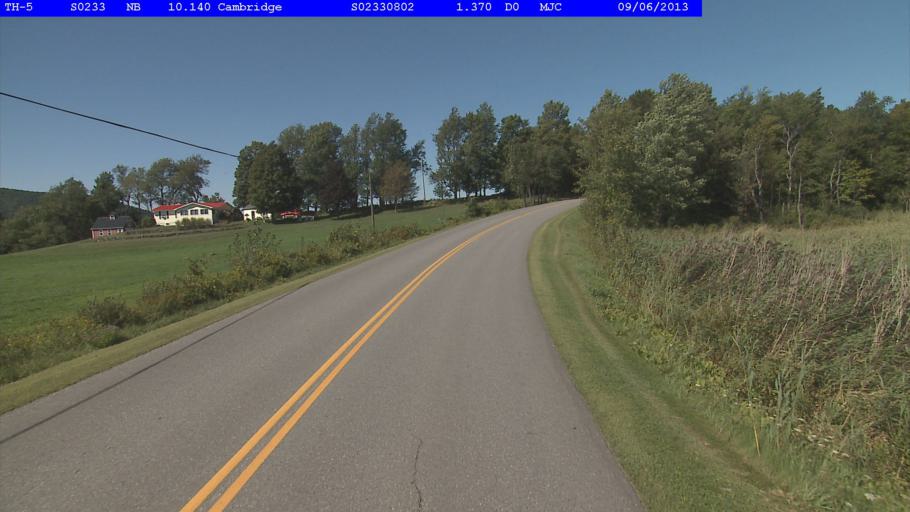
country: US
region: Vermont
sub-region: Chittenden County
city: Jericho
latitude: 44.6015
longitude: -72.8569
